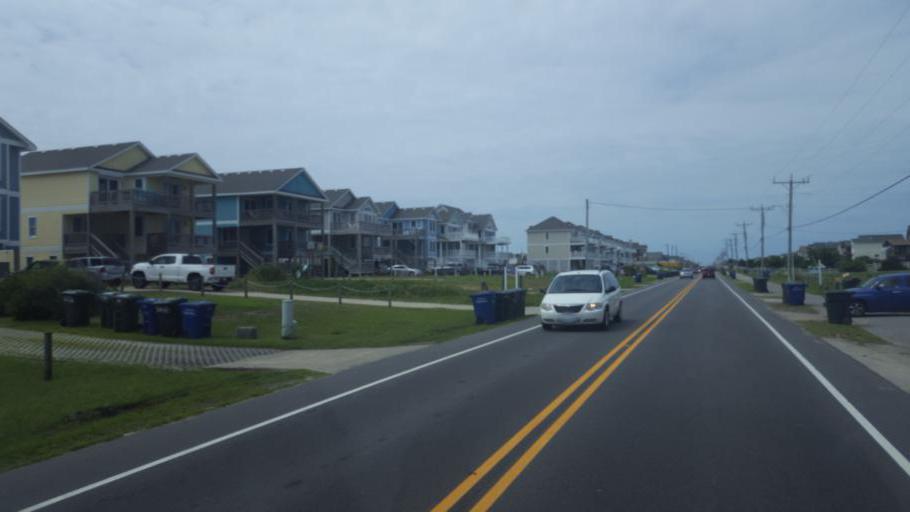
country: US
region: North Carolina
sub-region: Dare County
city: Nags Head
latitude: 35.9655
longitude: -75.6287
